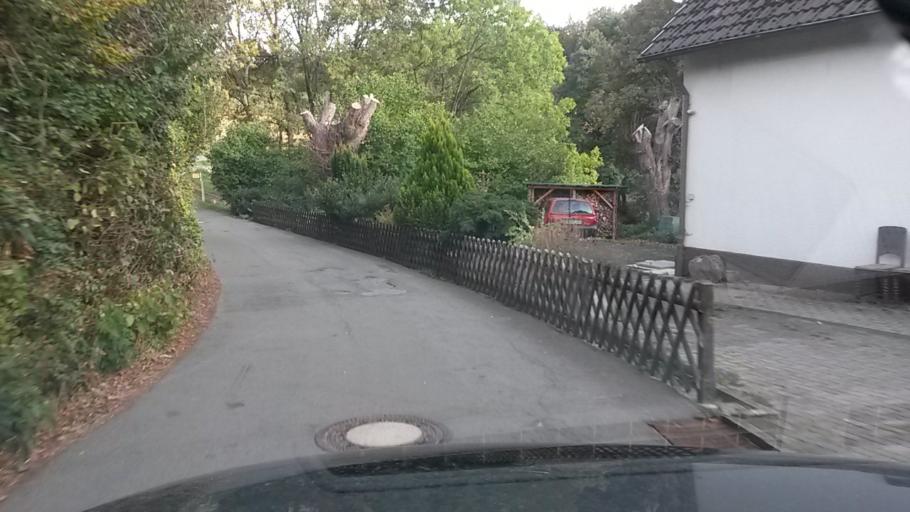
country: DE
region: North Rhine-Westphalia
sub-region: Regierungsbezirk Arnsberg
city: Herscheid
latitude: 51.2125
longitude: 7.7583
